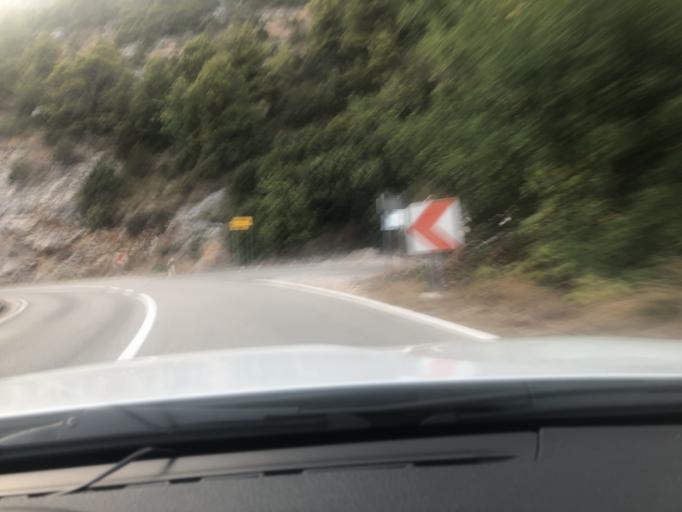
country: HR
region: Splitsko-Dalmatinska
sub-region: Grad Hvar
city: Hvar
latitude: 43.1658
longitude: 16.4902
